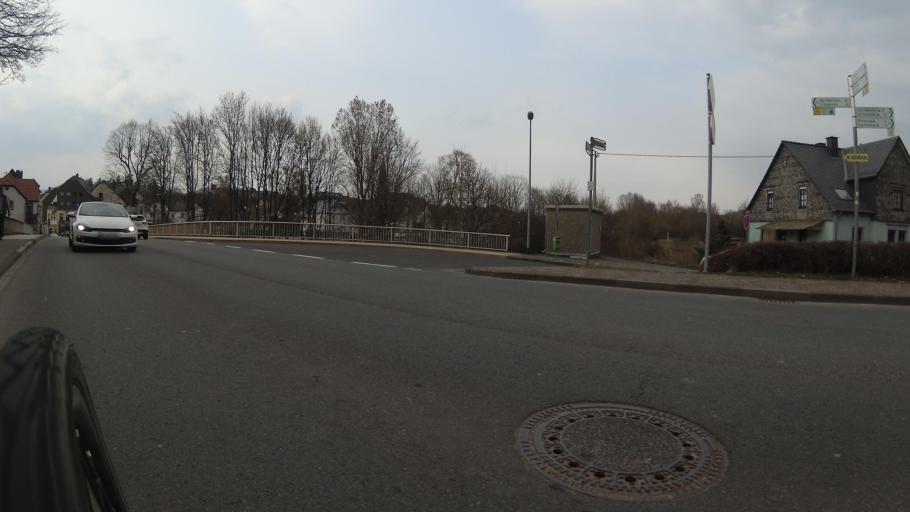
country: DE
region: Rheinland-Pfalz
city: Birkenfeld
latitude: 49.6450
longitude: 7.1688
